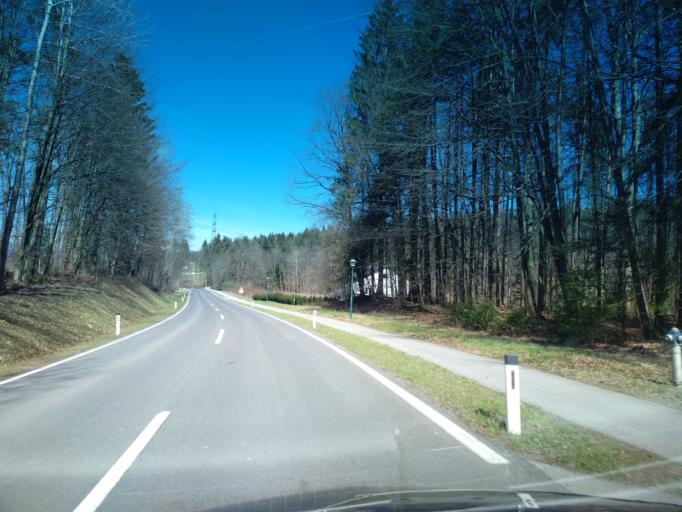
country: AT
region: Styria
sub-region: Politischer Bezirk Deutschlandsberg
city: Hollenegg
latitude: 46.7898
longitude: 15.2371
